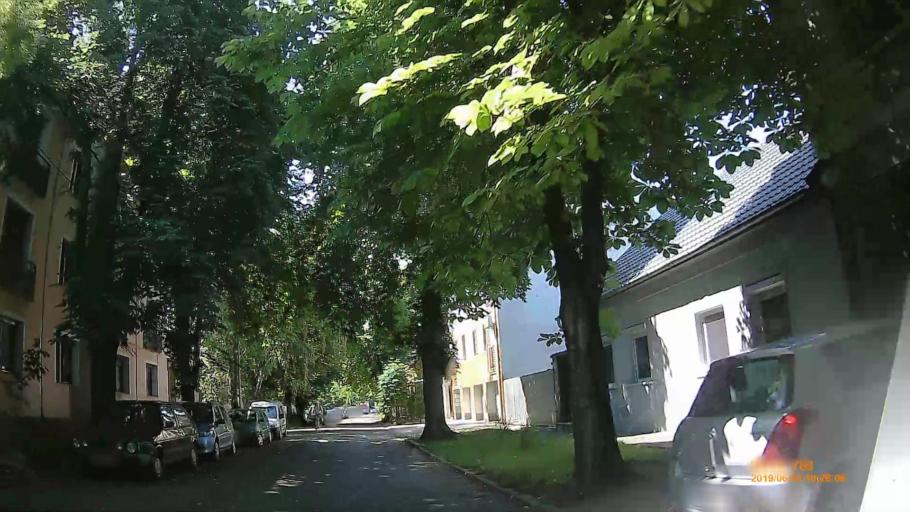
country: HU
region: Jasz-Nagykun-Szolnok
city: Szolnok
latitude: 47.1700
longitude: 20.1763
